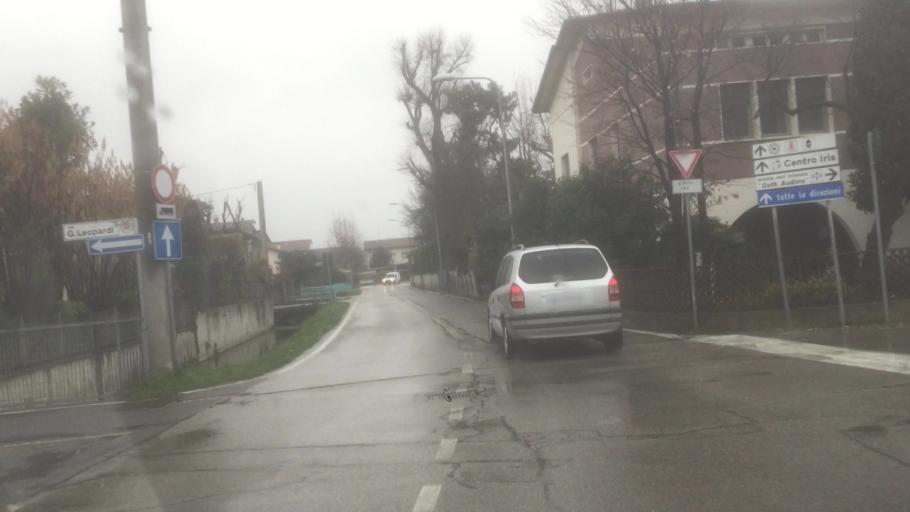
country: IT
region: Lombardy
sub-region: Provincia di Mantova
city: Castel Goffredo
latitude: 45.2963
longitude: 10.4706
